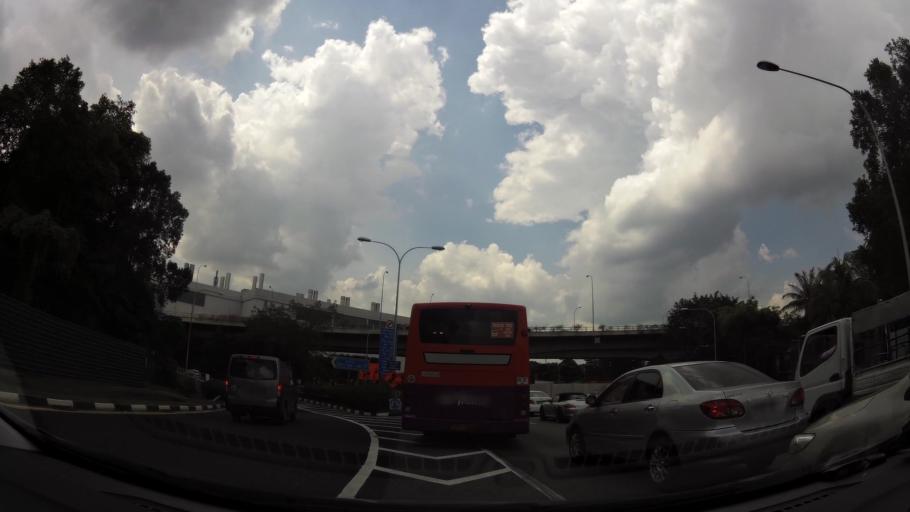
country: MY
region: Johor
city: Johor Bahru
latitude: 1.4396
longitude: 103.7692
